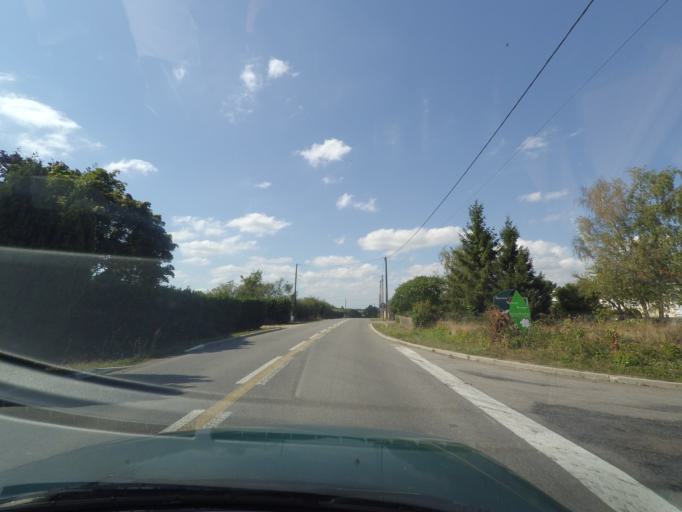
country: FR
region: Pays de la Loire
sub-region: Departement de la Loire-Atlantique
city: Sainte-Pazanne
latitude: 47.0767
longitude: -1.7857
